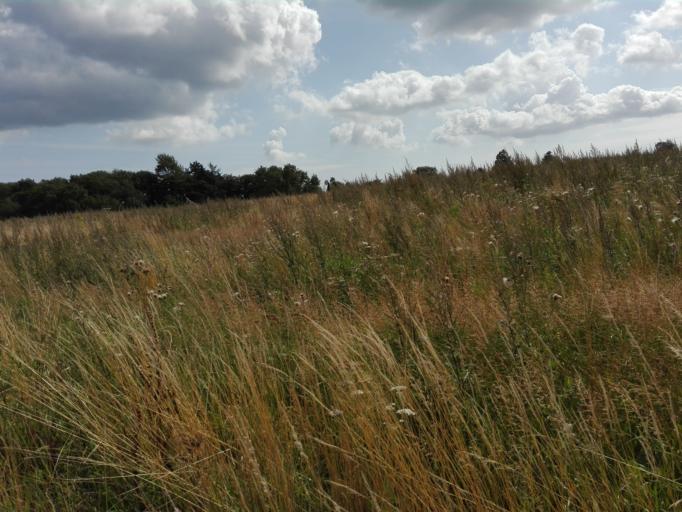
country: DK
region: Central Jutland
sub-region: Arhus Kommune
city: Beder
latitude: 56.0493
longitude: 10.2624
